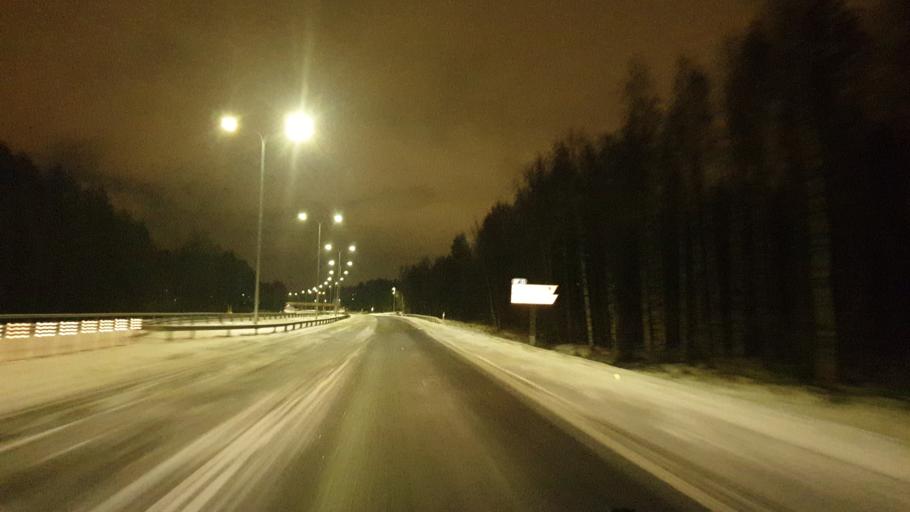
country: FI
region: Northern Ostrobothnia
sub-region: Oulu
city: Oulu
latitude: 65.0448
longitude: 25.4648
